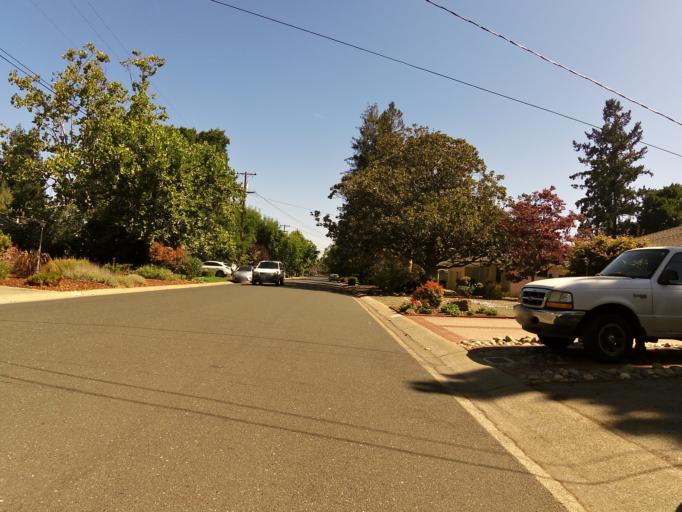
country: US
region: California
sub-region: Santa Clara County
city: Los Altos
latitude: 37.3933
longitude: -122.1078
